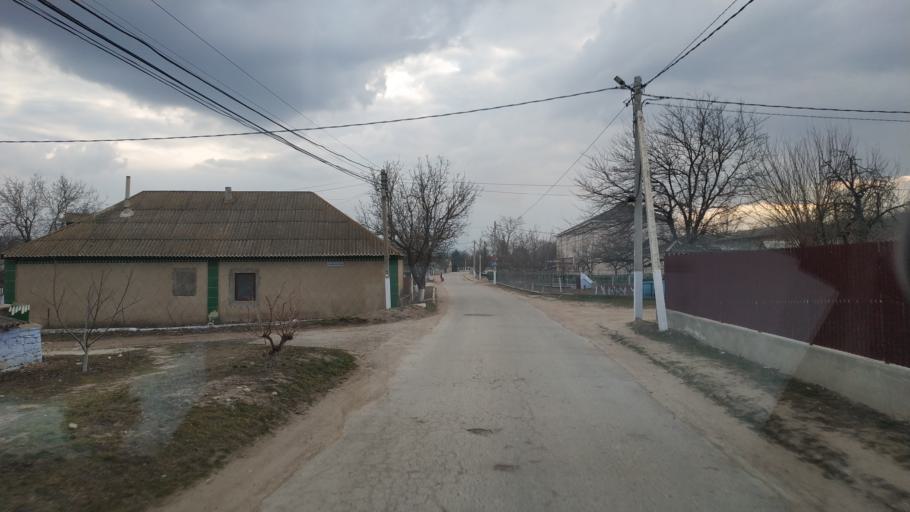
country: MD
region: Telenesti
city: Grigoriopol
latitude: 47.0215
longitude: 29.3577
